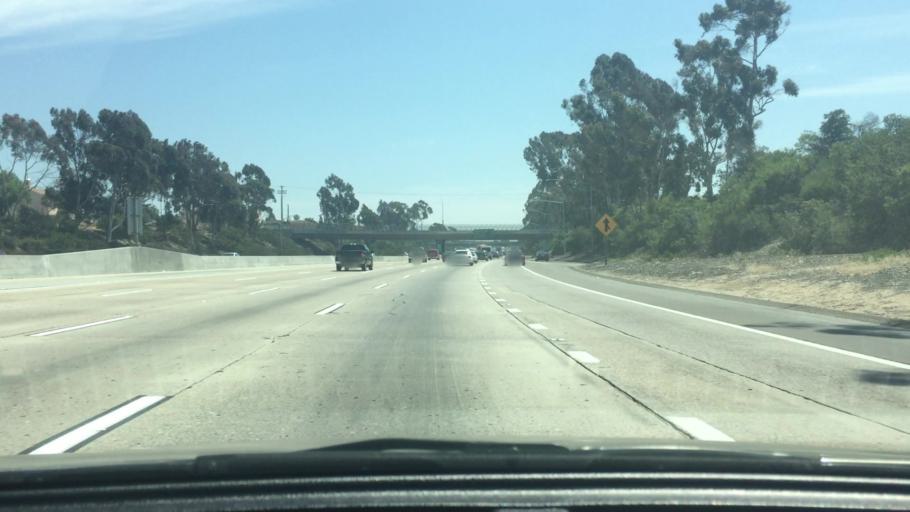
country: US
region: California
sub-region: San Diego County
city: National City
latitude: 32.7030
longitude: -117.0950
